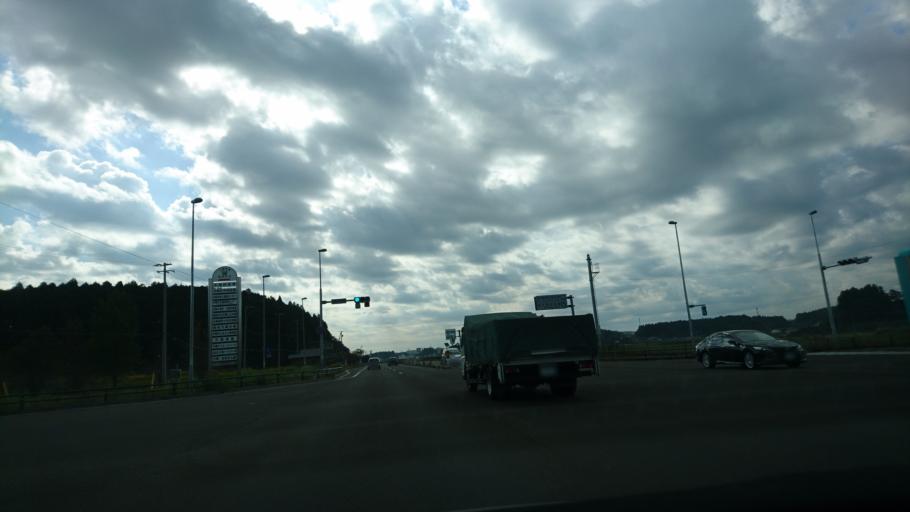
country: JP
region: Miyagi
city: Tomiya
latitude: 38.4659
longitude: 140.8767
